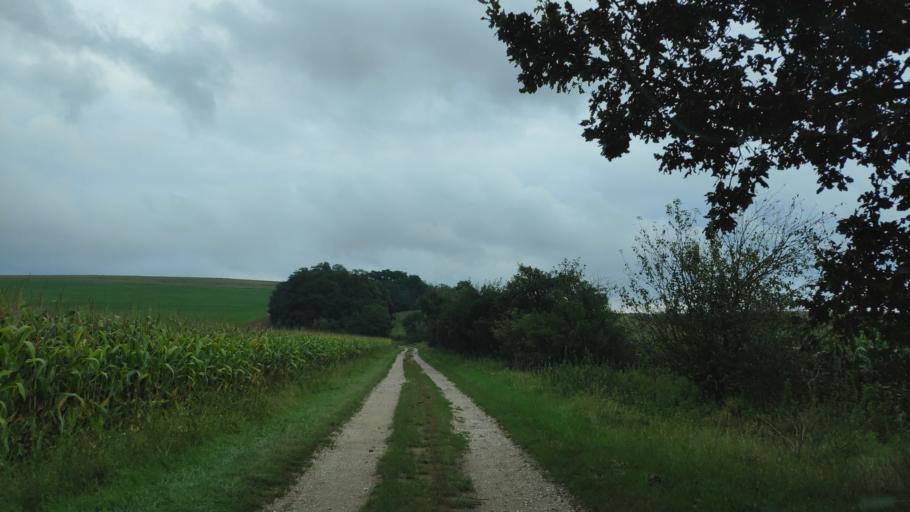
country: SK
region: Kosicky
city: Moldava nad Bodvou
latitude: 48.5790
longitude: 20.8996
